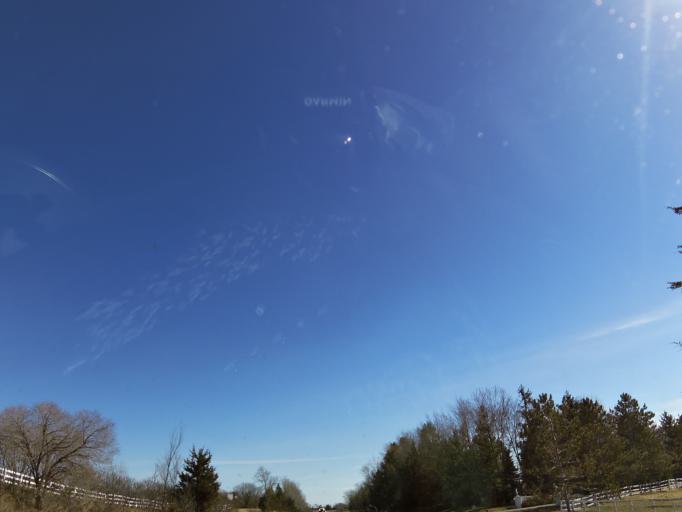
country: US
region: Minnesota
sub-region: Wright County
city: Rockford
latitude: 45.0987
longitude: -93.7718
